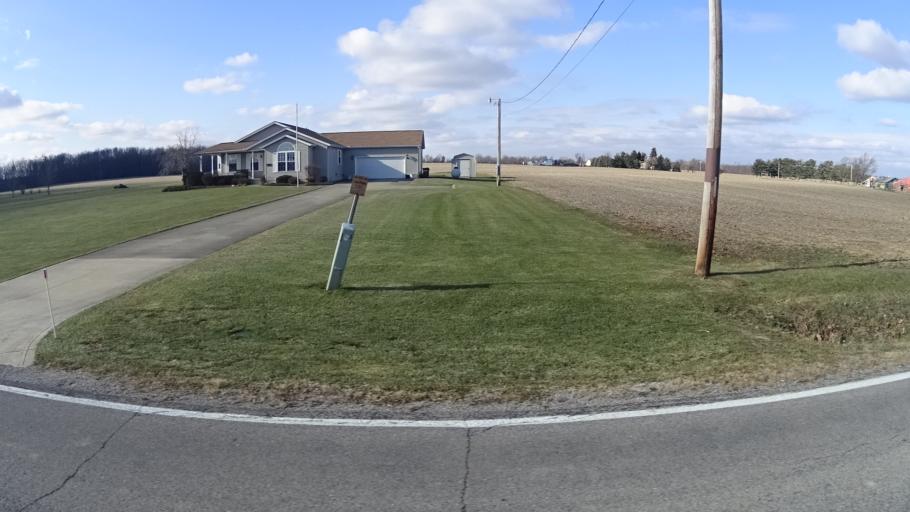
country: US
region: Ohio
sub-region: Lorain County
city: Camden
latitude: 41.2355
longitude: -82.2562
